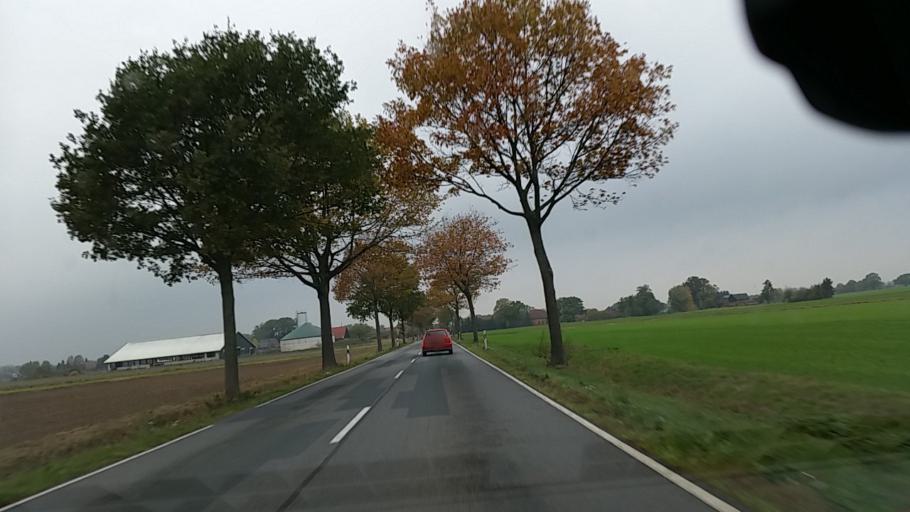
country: DE
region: Lower Saxony
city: Wittingen
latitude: 52.7063
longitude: 10.7766
